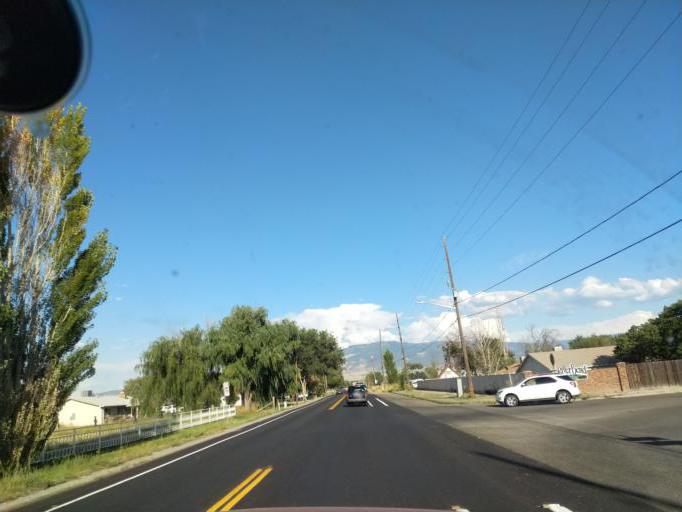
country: US
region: Colorado
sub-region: Mesa County
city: Fruitvale
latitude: 39.0629
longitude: -108.4767
